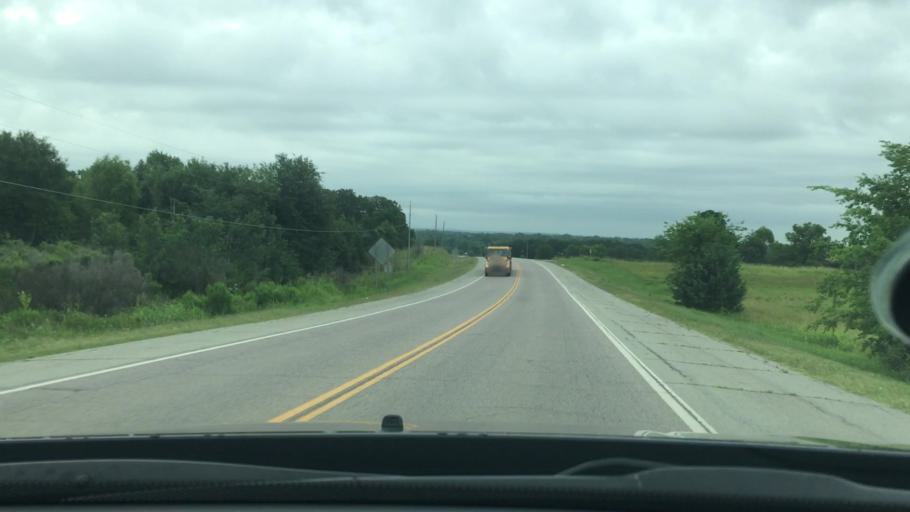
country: US
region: Oklahoma
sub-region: Coal County
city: Coalgate
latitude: 34.5546
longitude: -96.2393
